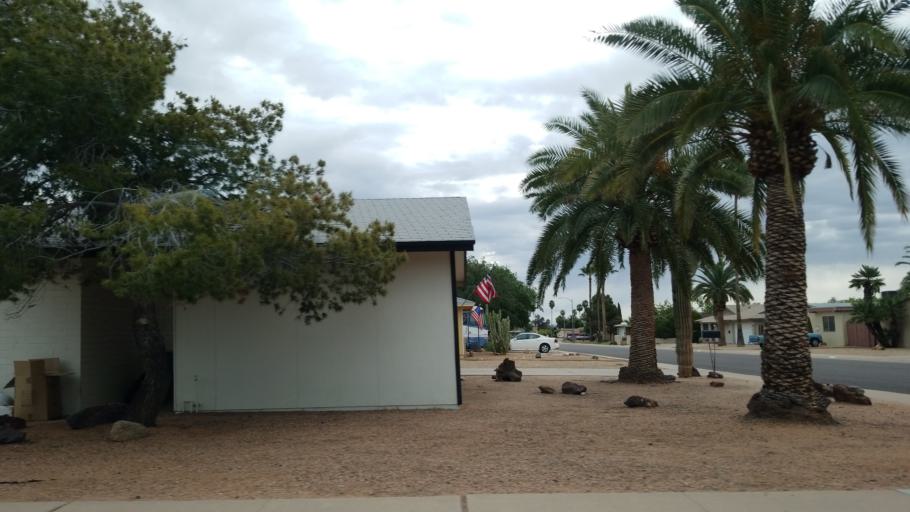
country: US
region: Arizona
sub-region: Maricopa County
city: Paradise Valley
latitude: 33.5992
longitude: -112.0305
